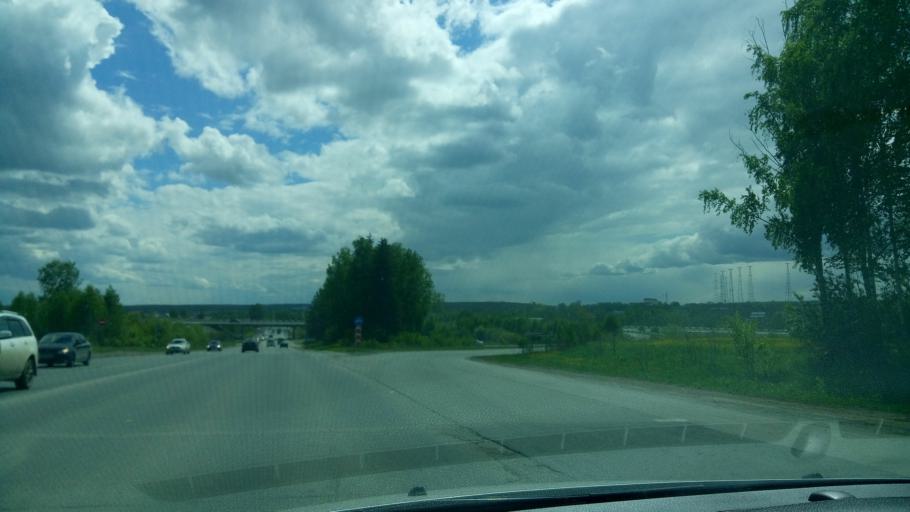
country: RU
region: Sverdlovsk
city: Verkhnyaya Pyshma
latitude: 56.9438
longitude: 60.6096
